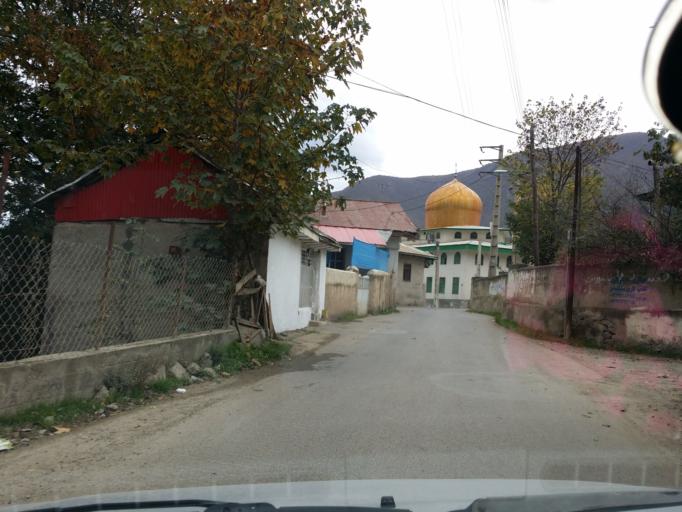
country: IR
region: Mazandaran
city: `Abbasabad
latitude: 36.5041
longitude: 51.1498
